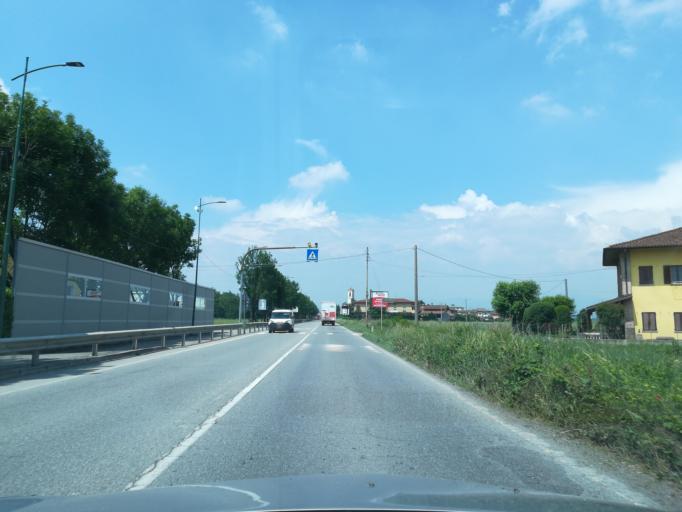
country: IT
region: Lombardy
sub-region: Provincia di Bergamo
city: Cavernago
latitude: 45.6263
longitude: 9.7690
